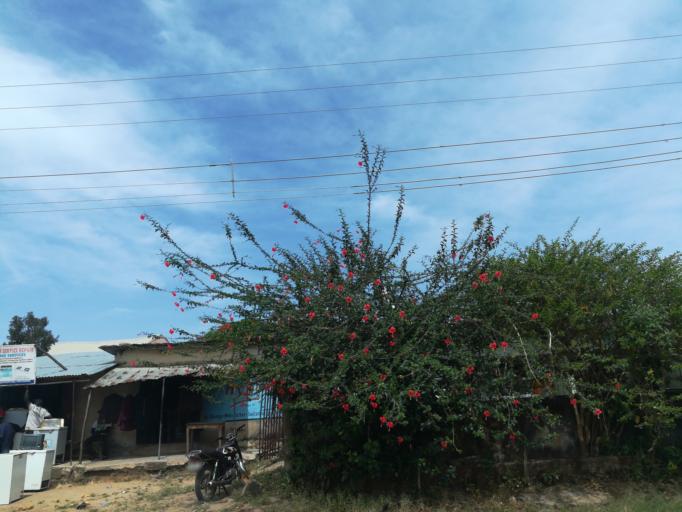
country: NG
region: Plateau
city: Jos
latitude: 9.9256
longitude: 8.8421
